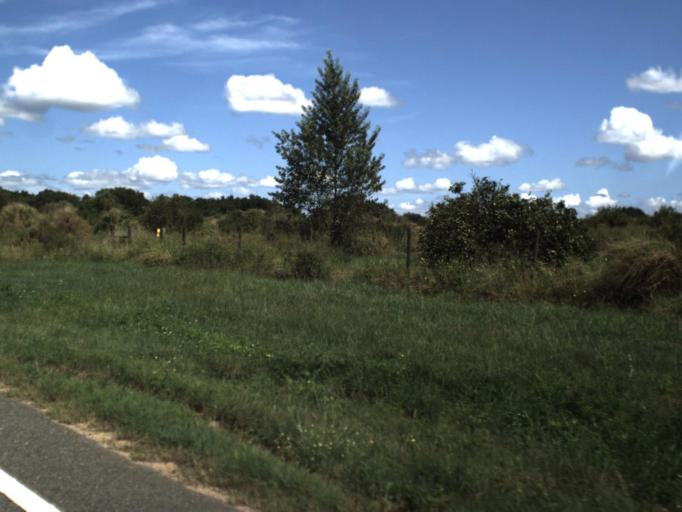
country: US
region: Florida
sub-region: Polk County
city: Lake Wales
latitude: 27.9477
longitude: -81.5948
